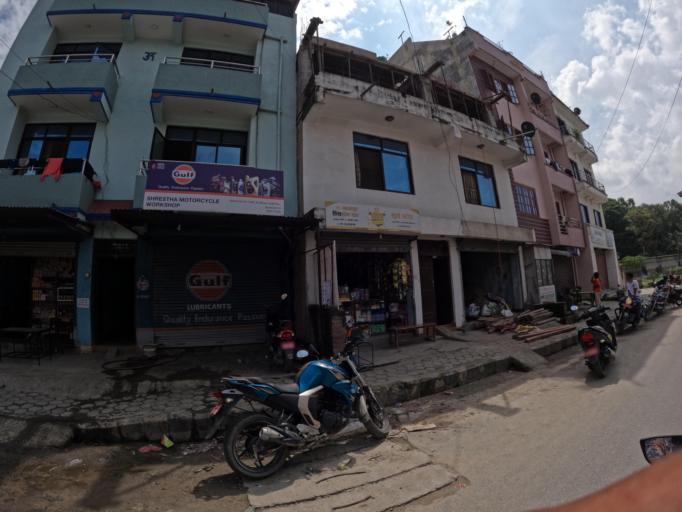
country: NP
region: Central Region
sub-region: Bagmati Zone
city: Bhaktapur
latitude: 27.6776
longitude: 85.3834
